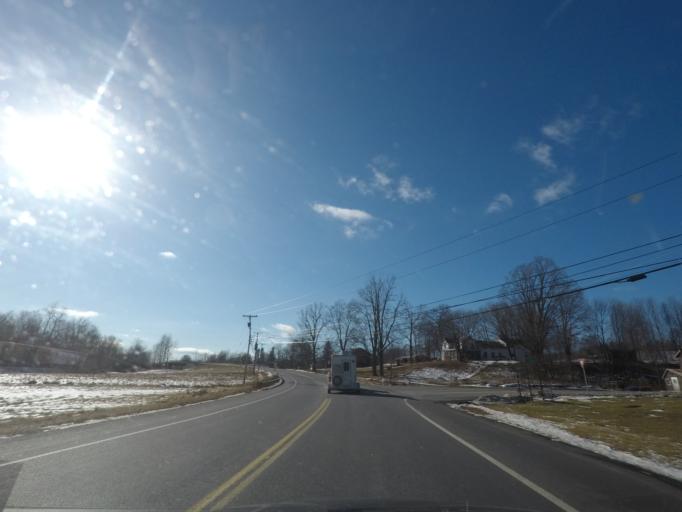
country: US
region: New York
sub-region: Columbia County
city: Chatham
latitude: 42.4198
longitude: -73.5076
